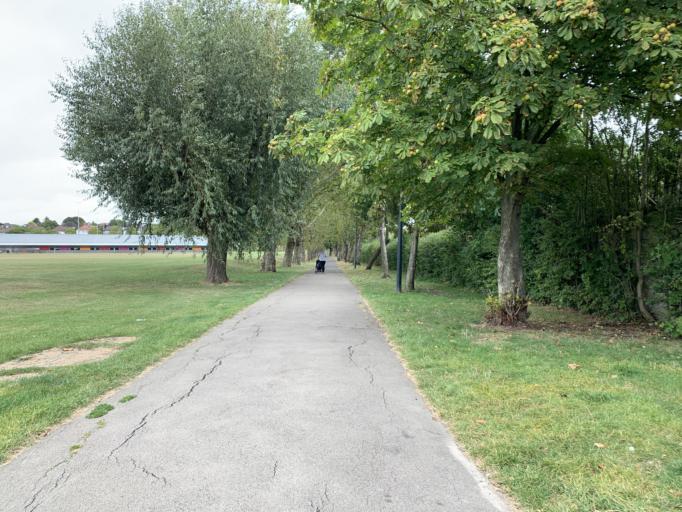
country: GB
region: England
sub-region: Greater London
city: Hammersmith
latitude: 51.5379
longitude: -0.2301
